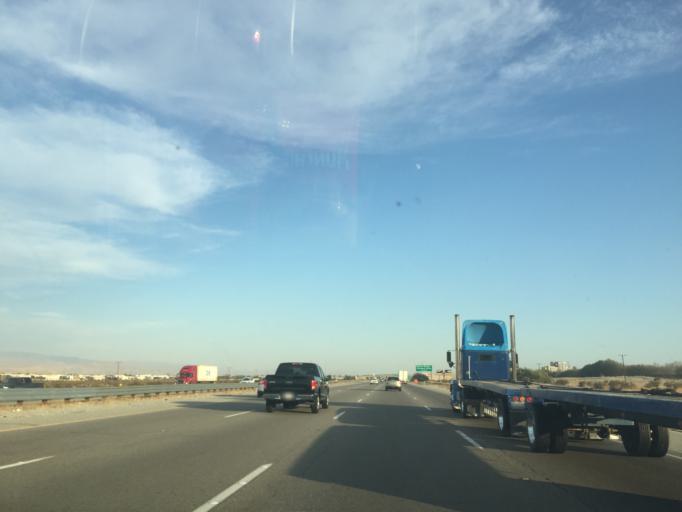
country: US
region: California
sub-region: Riverside County
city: Thousand Palms
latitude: 33.8277
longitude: -116.4221
